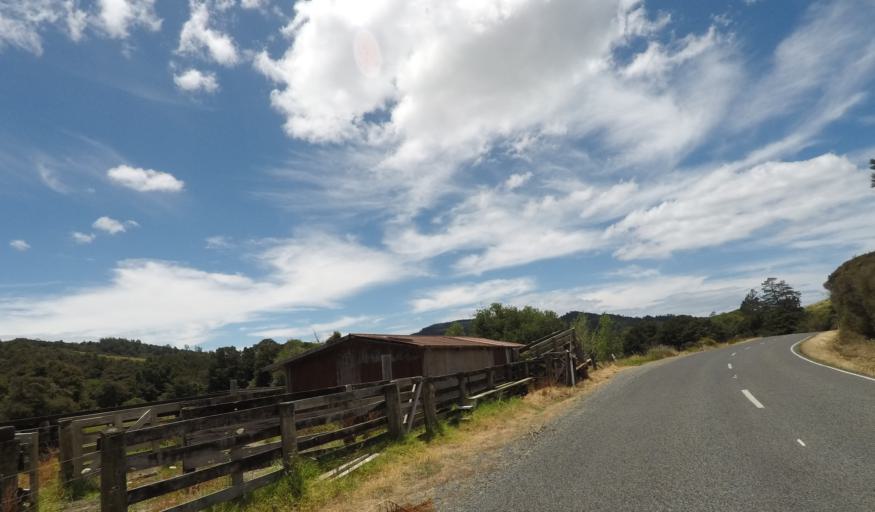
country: NZ
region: Northland
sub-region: Whangarei
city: Ngunguru
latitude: -35.5071
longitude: 174.4215
